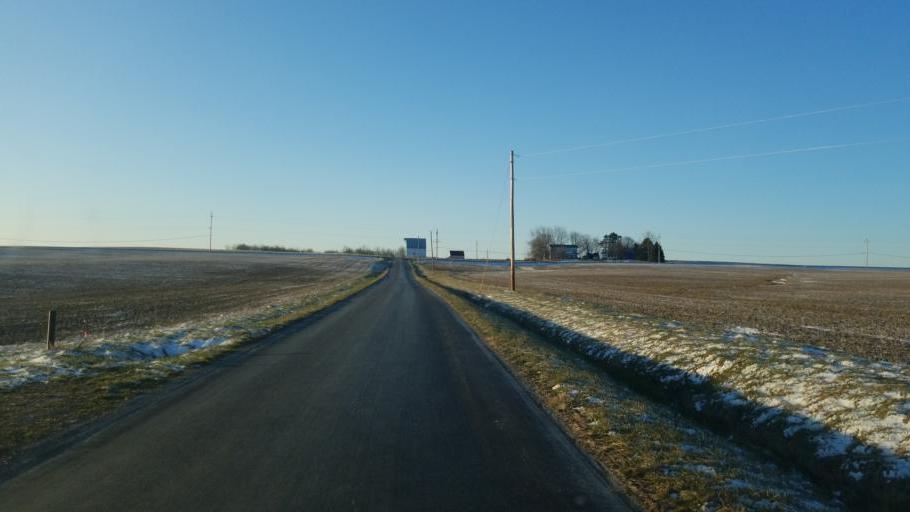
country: US
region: Ohio
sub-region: Highland County
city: Leesburg
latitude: 39.2430
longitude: -83.4977
